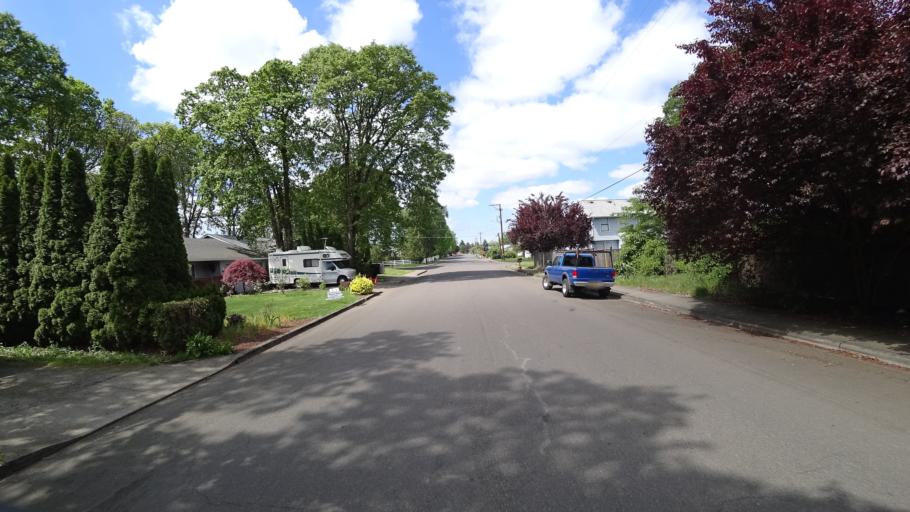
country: US
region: Oregon
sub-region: Washington County
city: Aloha
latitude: 45.5079
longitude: -122.8864
